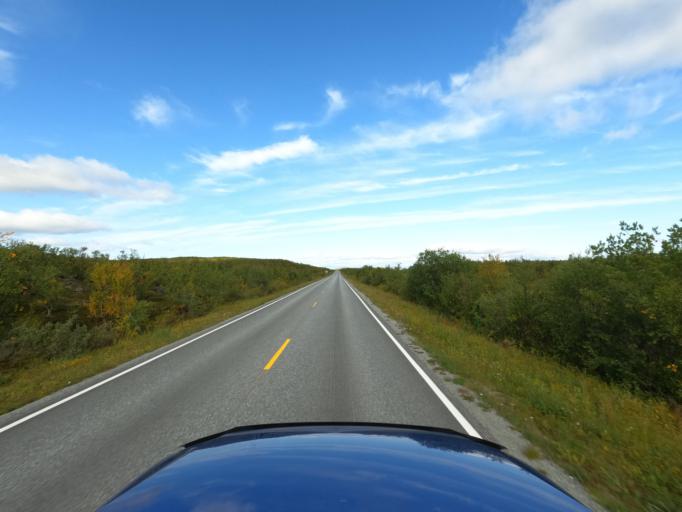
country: NO
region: Finnmark Fylke
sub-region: Karasjok
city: Karasjohka
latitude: 69.6806
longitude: 25.2629
